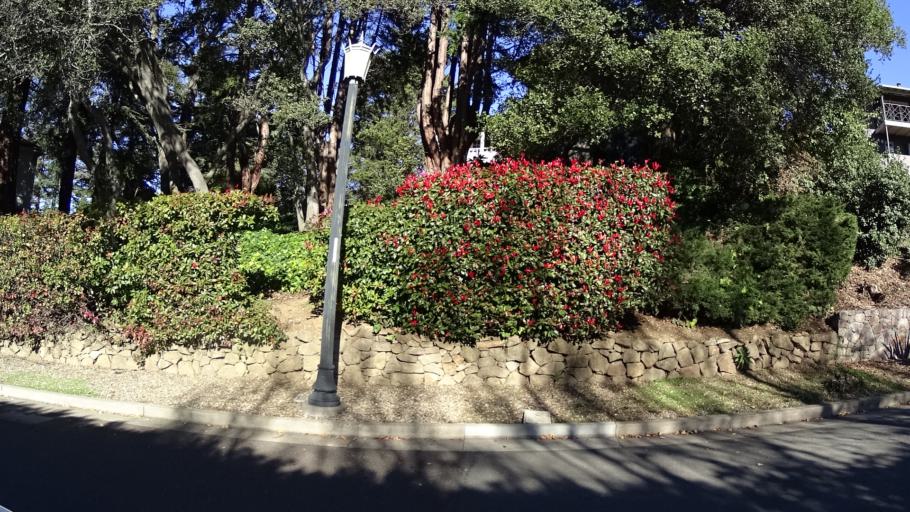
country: US
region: California
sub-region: Alameda County
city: Piedmont
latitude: 37.8305
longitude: -122.2183
